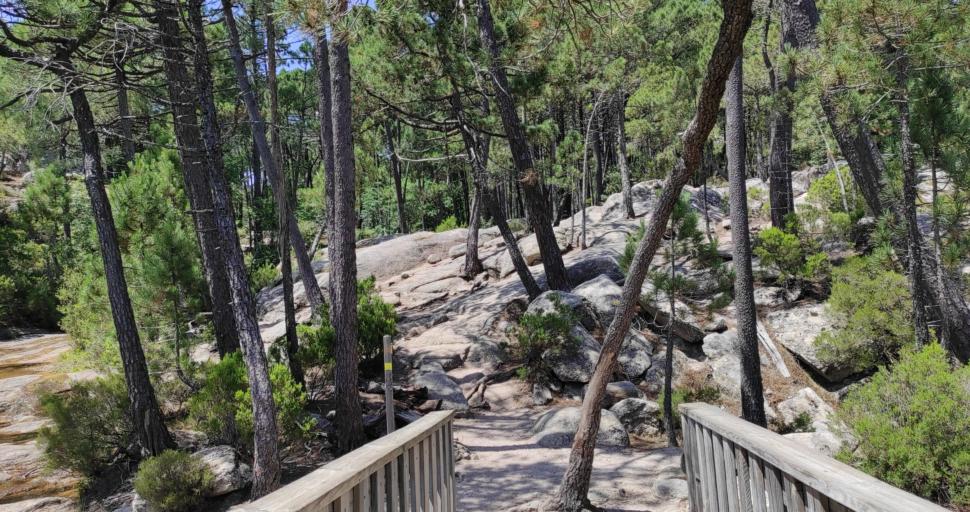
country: FR
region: Corsica
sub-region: Departement de la Corse-du-Sud
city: Zonza
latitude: 41.6862
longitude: 9.2013
